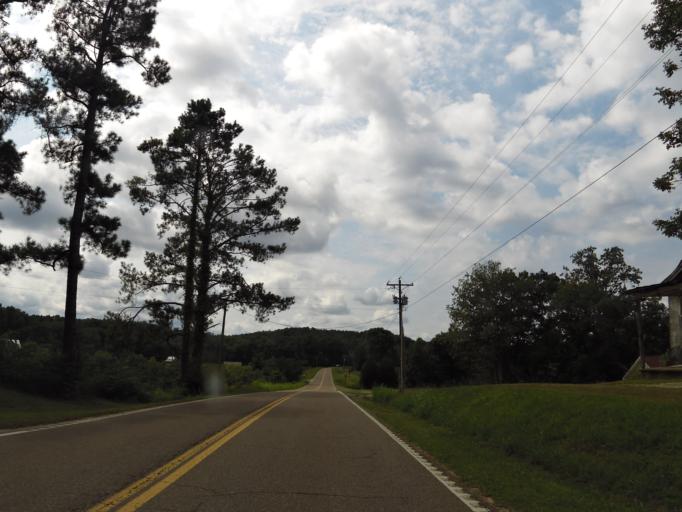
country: US
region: Tennessee
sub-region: Decatur County
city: Decaturville
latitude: 35.5864
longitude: -88.0602
